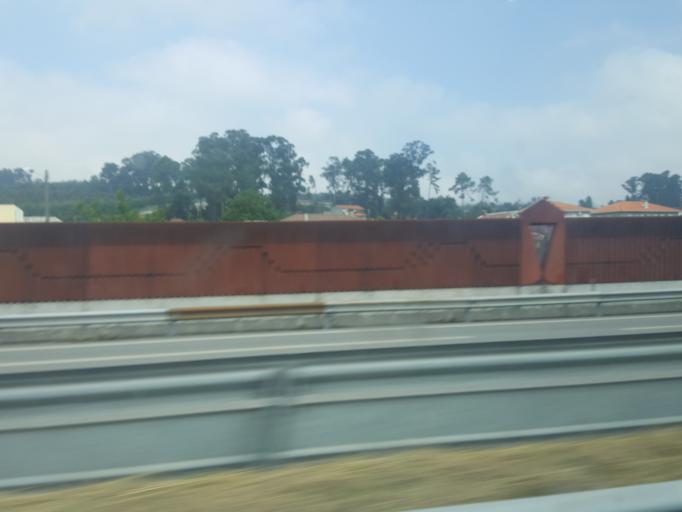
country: PT
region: Porto
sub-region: Lousada
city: Meinedo
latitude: 41.2243
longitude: -8.2338
